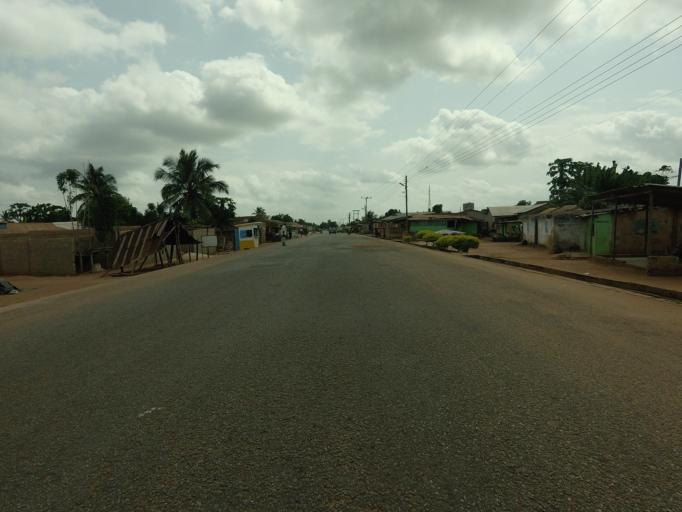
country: TG
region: Maritime
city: Lome
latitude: 6.2214
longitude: 1.0393
